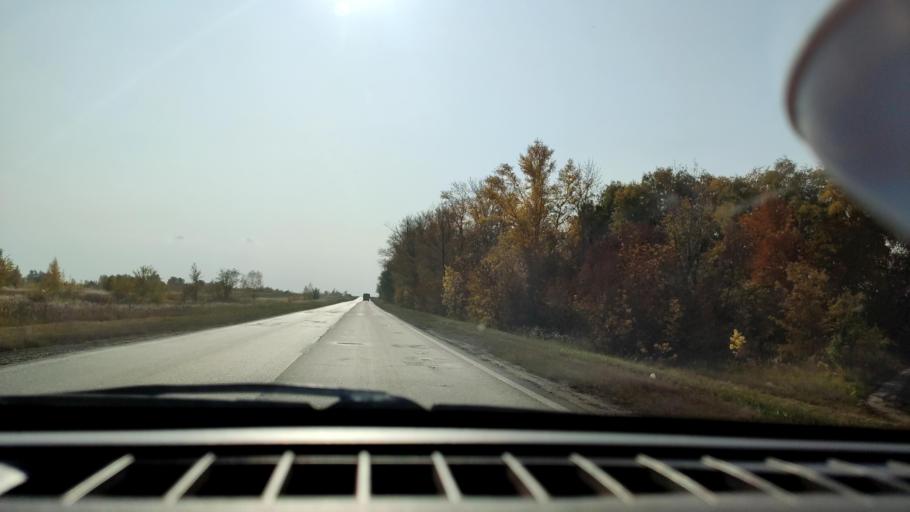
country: RU
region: Samara
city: Smyshlyayevka
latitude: 53.1201
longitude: 50.3661
